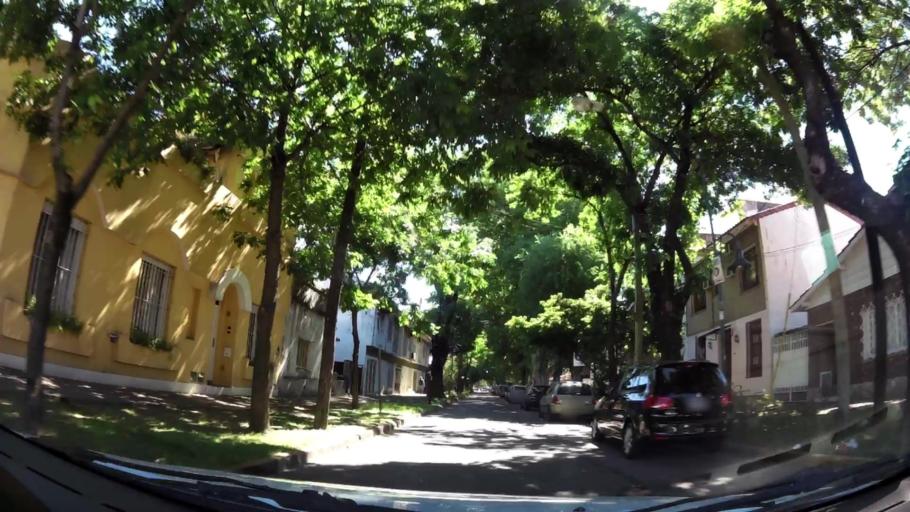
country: AR
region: Buenos Aires
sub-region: Partido de Vicente Lopez
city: Olivos
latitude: -34.5198
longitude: -58.4894
